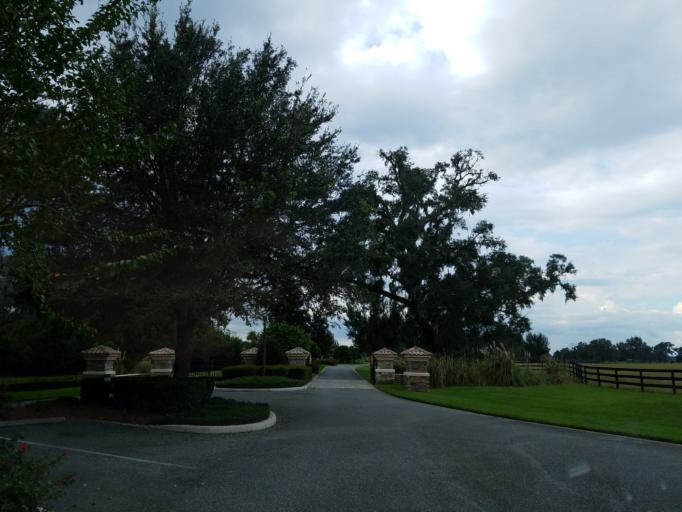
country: US
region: Florida
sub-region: Citrus County
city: Hernando
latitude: 29.0167
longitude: -82.3223
